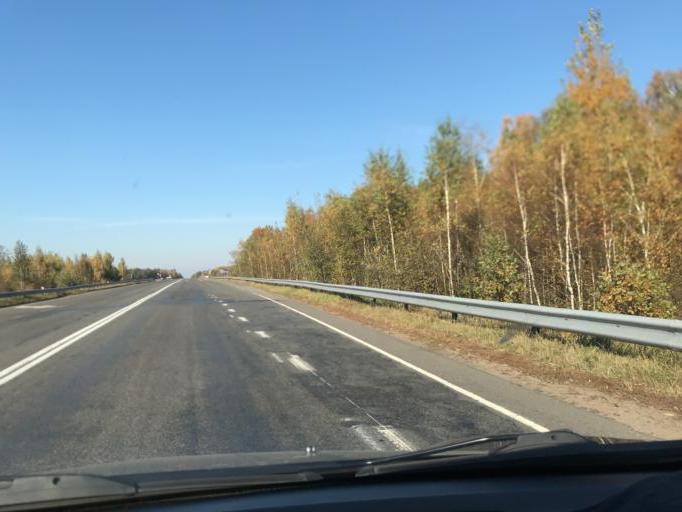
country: BY
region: Mogilev
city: Babruysk
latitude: 53.1007
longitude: 29.0579
